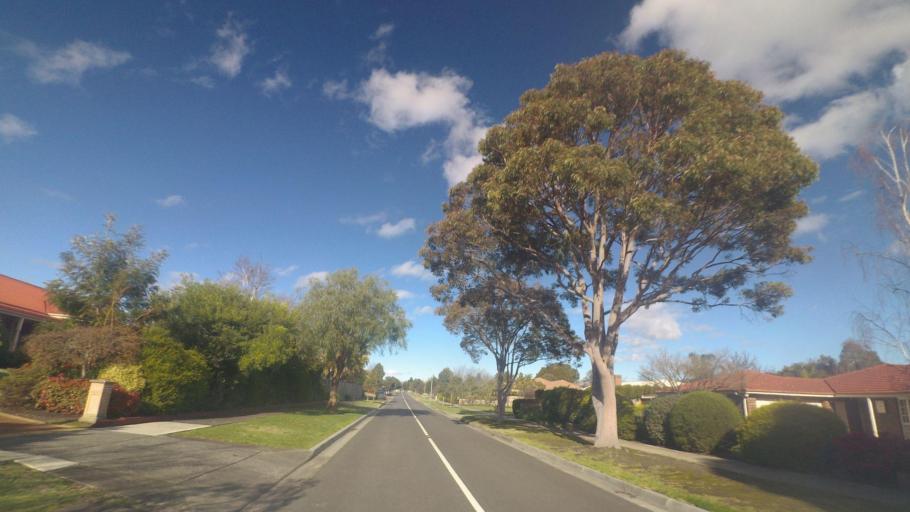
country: AU
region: Victoria
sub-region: Yarra Ranges
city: Lysterfield
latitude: -37.9117
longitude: 145.2810
